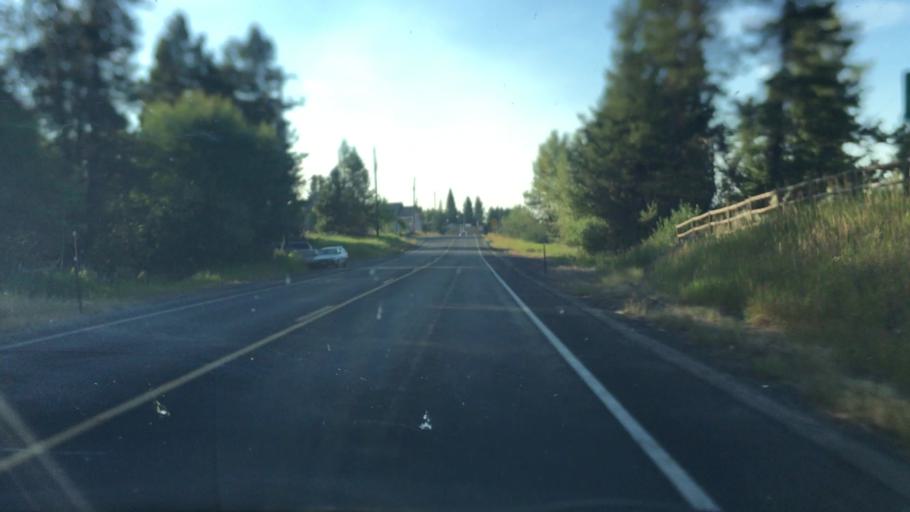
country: US
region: Idaho
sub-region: Valley County
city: McCall
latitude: 44.8294
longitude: -116.0824
